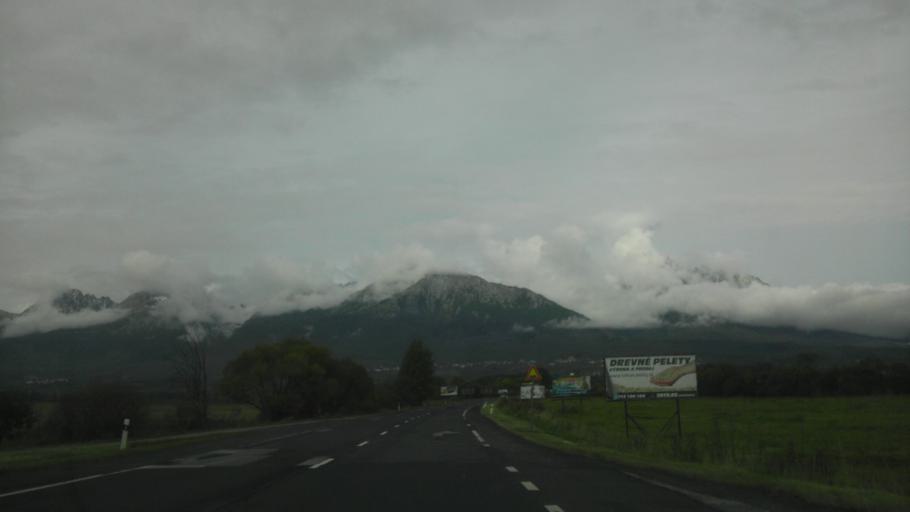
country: SK
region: Presovsky
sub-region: Okres Poprad
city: Nova Lesna
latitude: 49.0854
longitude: 20.2651
